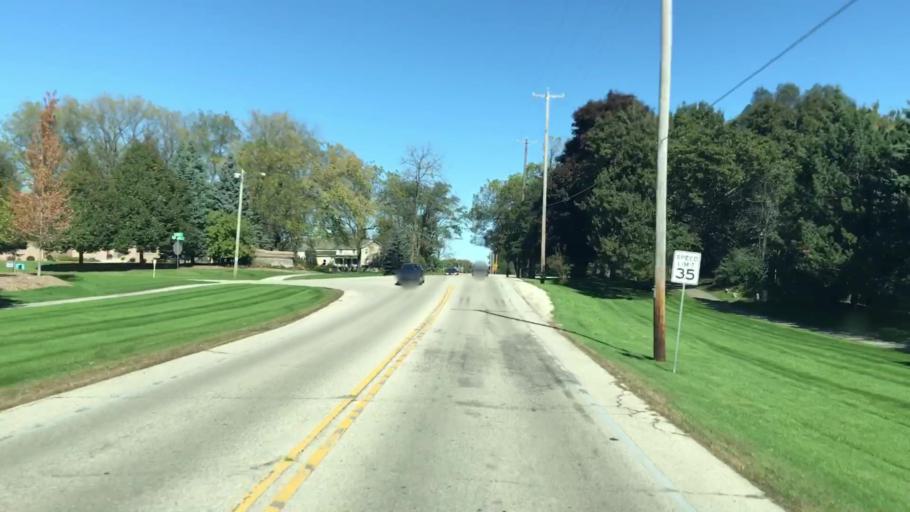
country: US
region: Wisconsin
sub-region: Waukesha County
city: Brookfield
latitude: 43.0690
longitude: -88.1662
